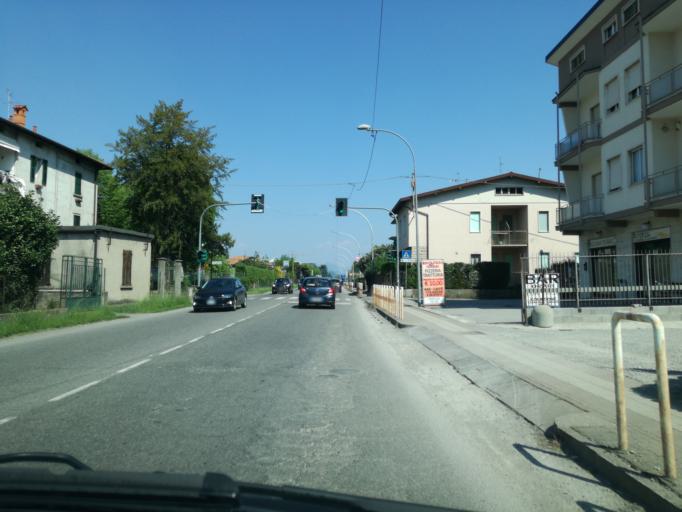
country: IT
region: Lombardy
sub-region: Provincia di Bergamo
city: Terno d'Isola
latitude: 45.6866
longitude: 9.5359
